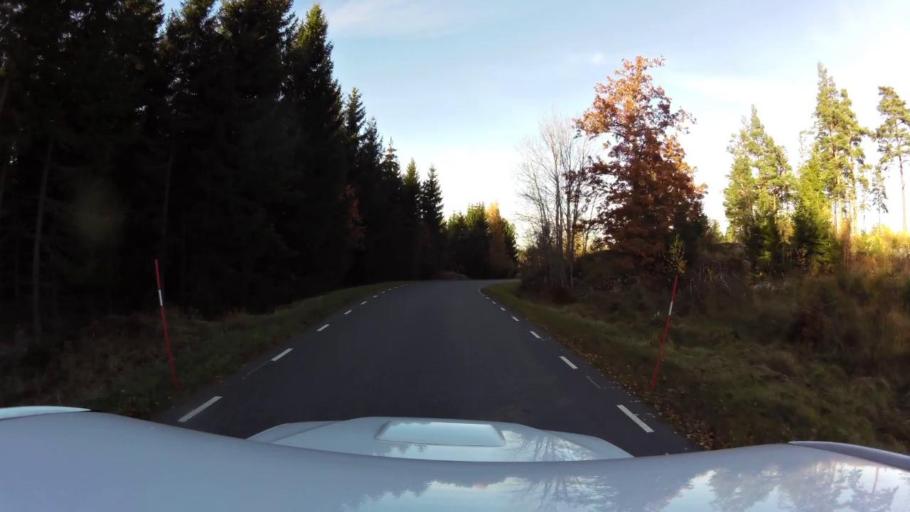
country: SE
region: OEstergoetland
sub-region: Linkopings Kommun
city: Sturefors
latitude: 58.2700
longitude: 15.6647
